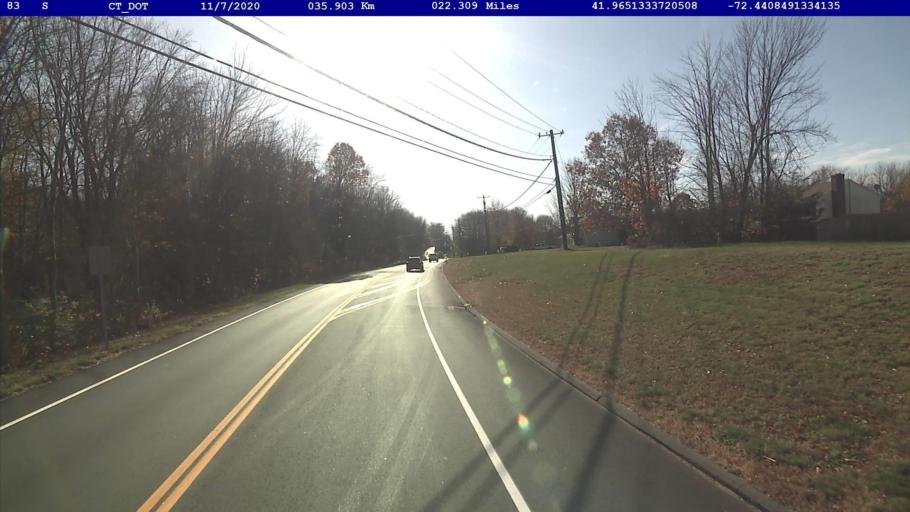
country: US
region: Connecticut
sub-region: Tolland County
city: Somers
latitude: 41.9651
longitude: -72.4409
